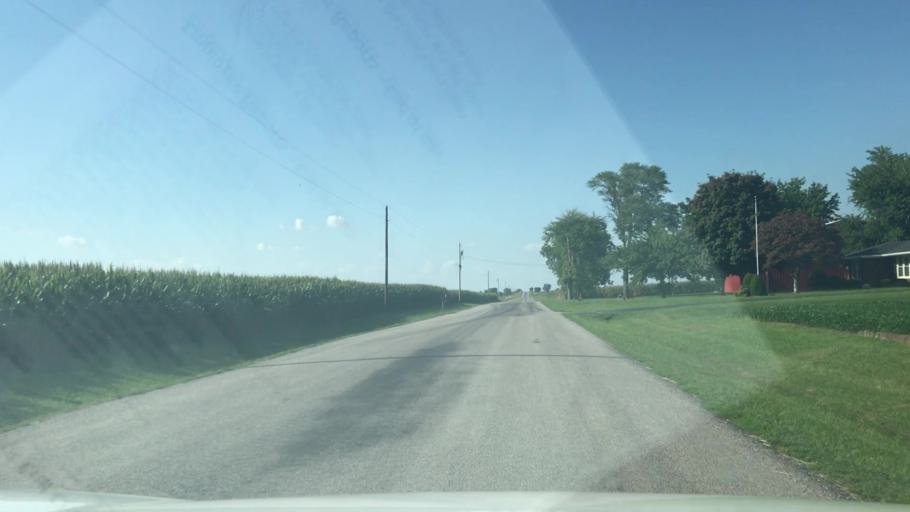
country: US
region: Illinois
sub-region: Washington County
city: Okawville
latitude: 38.4169
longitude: -89.4776
